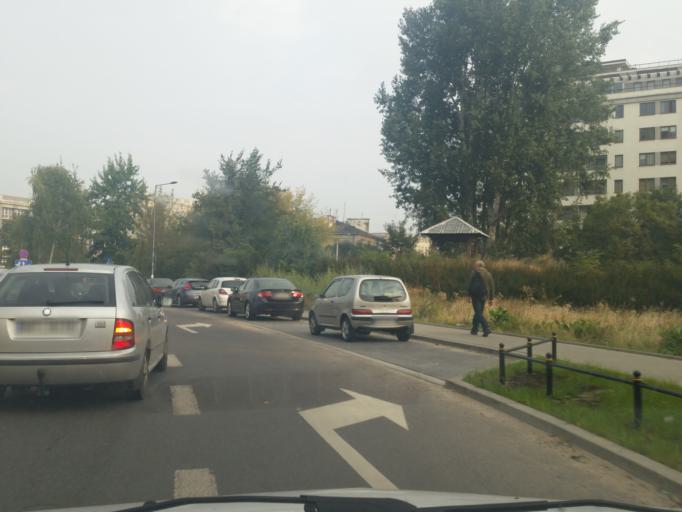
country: PL
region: Masovian Voivodeship
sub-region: Warszawa
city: Mokotow
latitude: 52.1828
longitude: 21.0256
